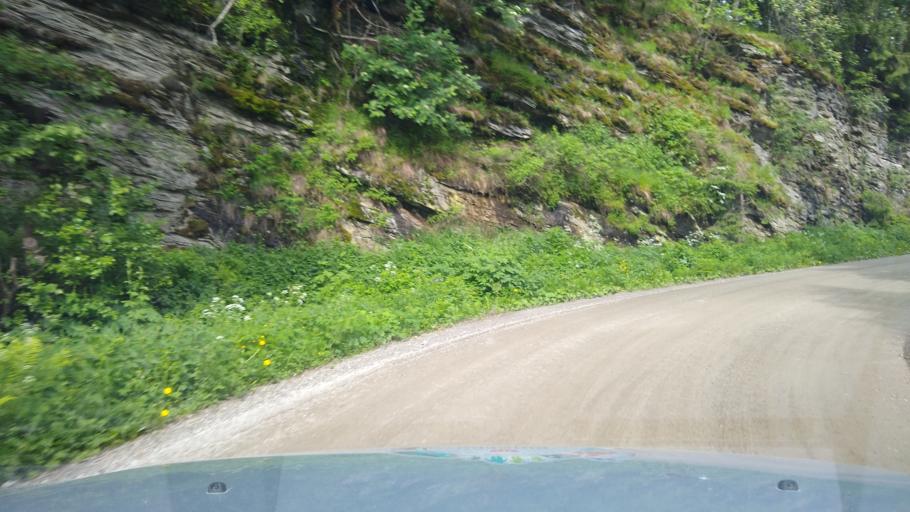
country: NO
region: Oppland
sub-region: Ringebu
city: Ringebu
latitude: 61.5161
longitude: 10.1320
